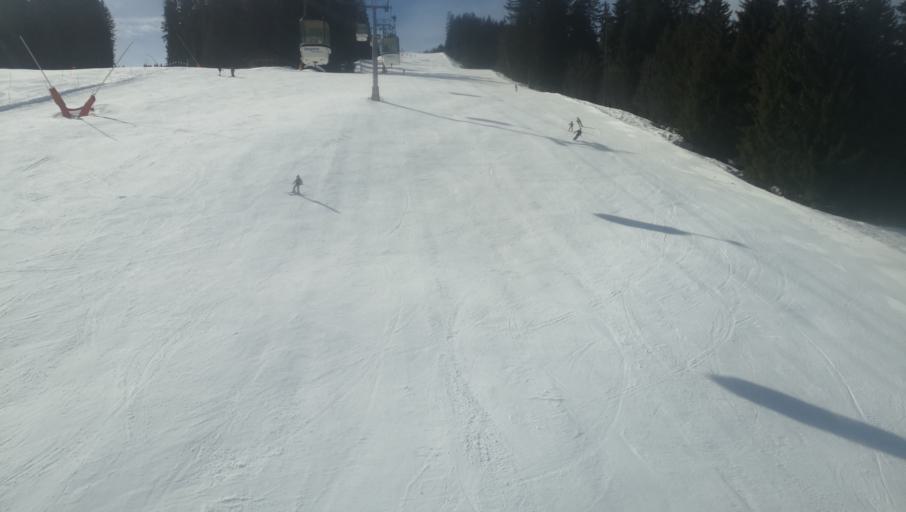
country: FR
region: Rhone-Alpes
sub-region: Departement de la Haute-Savoie
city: Megeve
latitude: 45.8434
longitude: 6.6239
